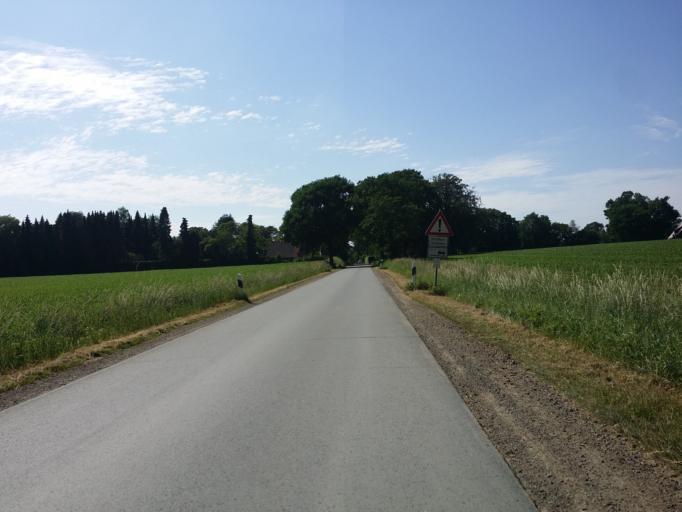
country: DE
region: Lower Saxony
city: Rastede
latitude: 53.2094
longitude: 8.2661
